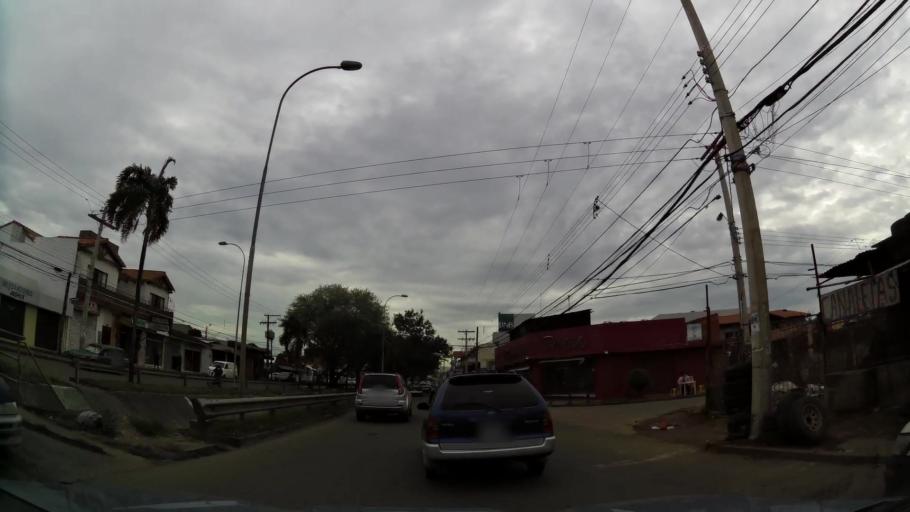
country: BO
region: Santa Cruz
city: Santa Cruz de la Sierra
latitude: -17.7670
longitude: -63.1629
